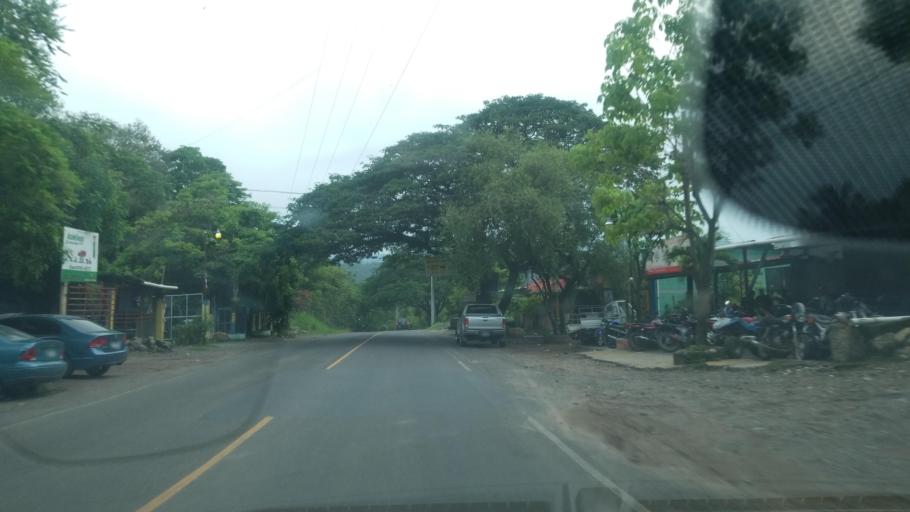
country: HN
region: Santa Barbara
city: Santa Barbara
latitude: 14.9194
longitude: -88.2474
